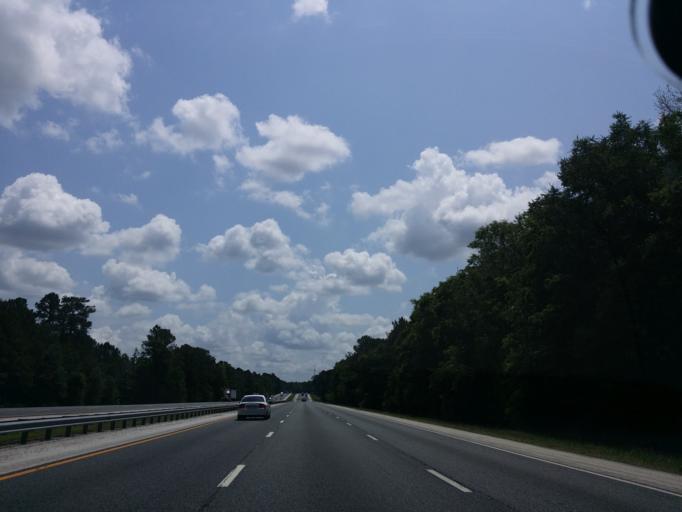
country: US
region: Florida
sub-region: Marion County
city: Citra
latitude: 29.3661
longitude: -82.2263
